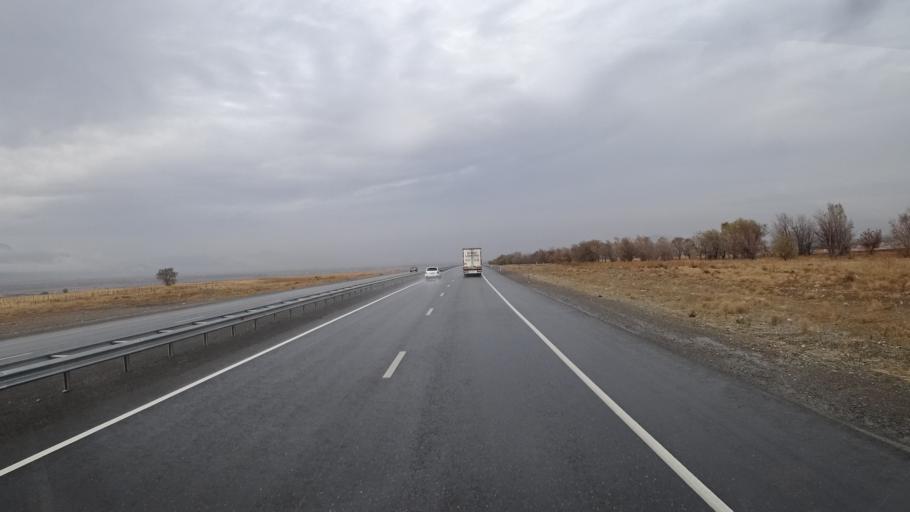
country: KZ
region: Ongtustik Qazaqstan
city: Turar Ryskulov
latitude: 42.5125
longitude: 70.3833
